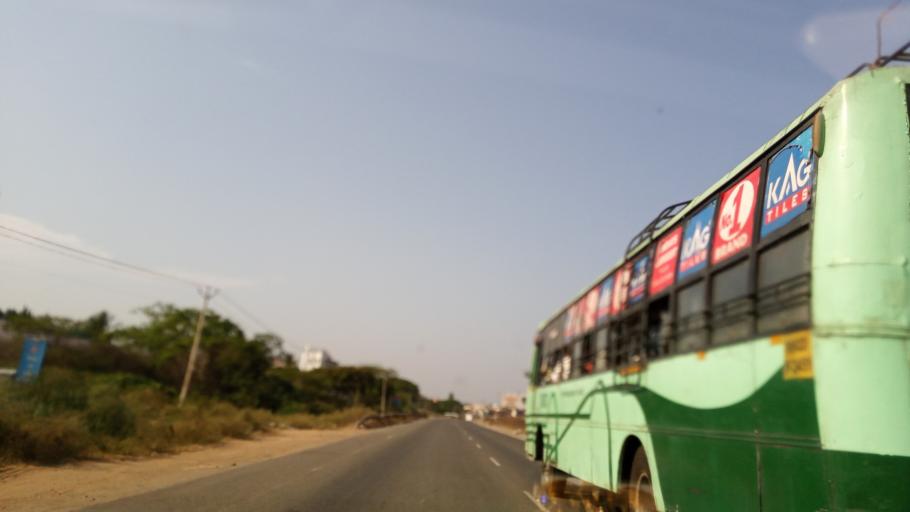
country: IN
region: Tamil Nadu
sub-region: Kancheepuram
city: Sriperumbudur
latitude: 12.9704
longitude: 79.9549
